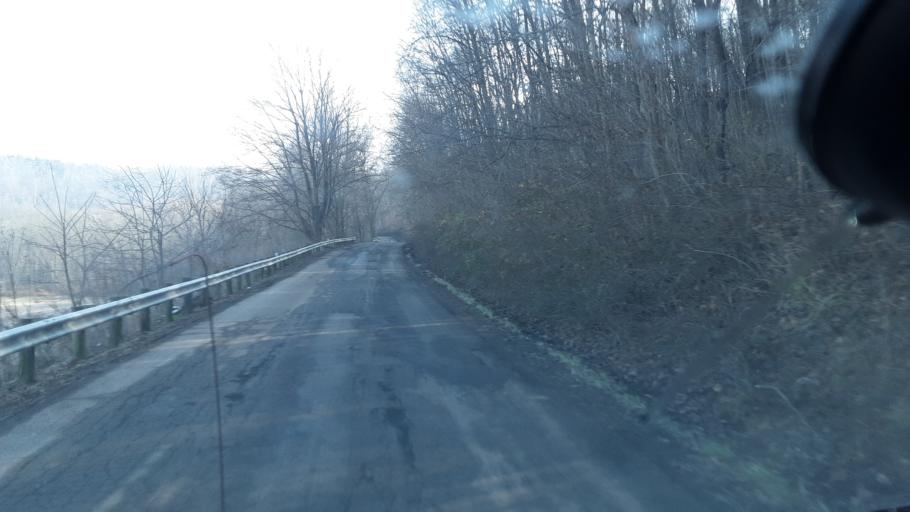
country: US
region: Ohio
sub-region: Knox County
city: Oak Hill
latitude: 40.4262
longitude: -82.1993
